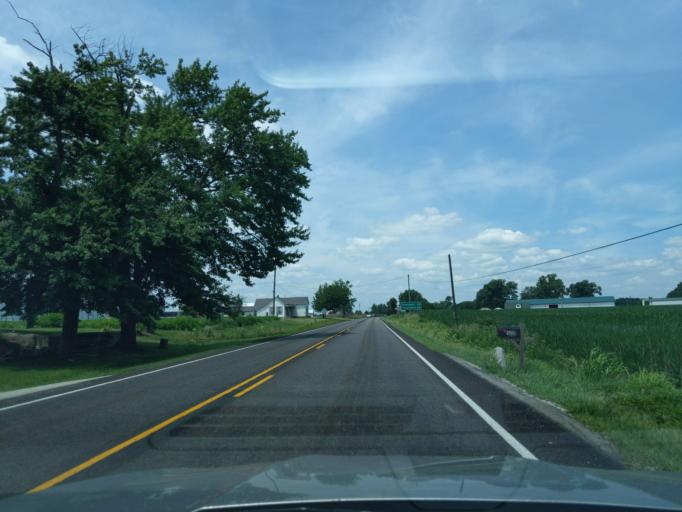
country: US
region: Indiana
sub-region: Ripley County
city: Osgood
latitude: 39.2090
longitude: -85.3311
